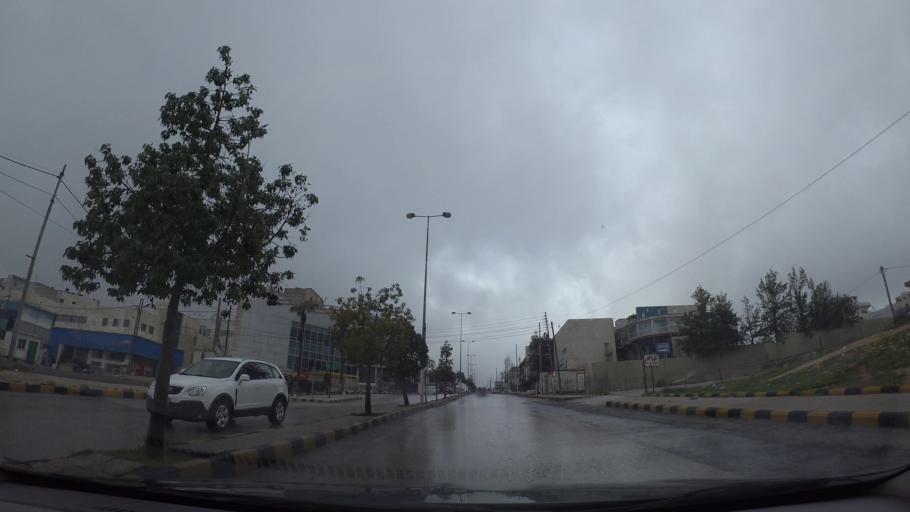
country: JO
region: Amman
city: Al Bunayyat ash Shamaliyah
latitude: 31.9410
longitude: 35.8855
